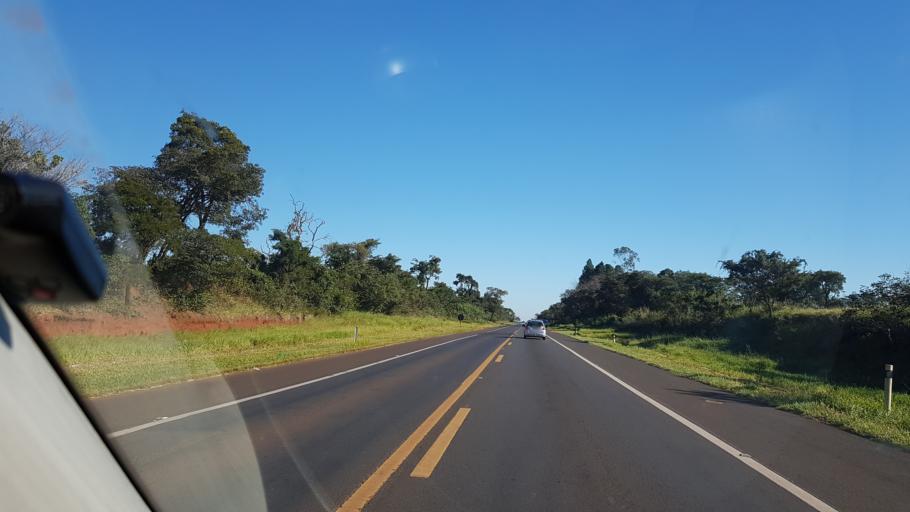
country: BR
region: Sao Paulo
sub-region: Assis
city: Assis
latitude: -22.6228
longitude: -50.4509
